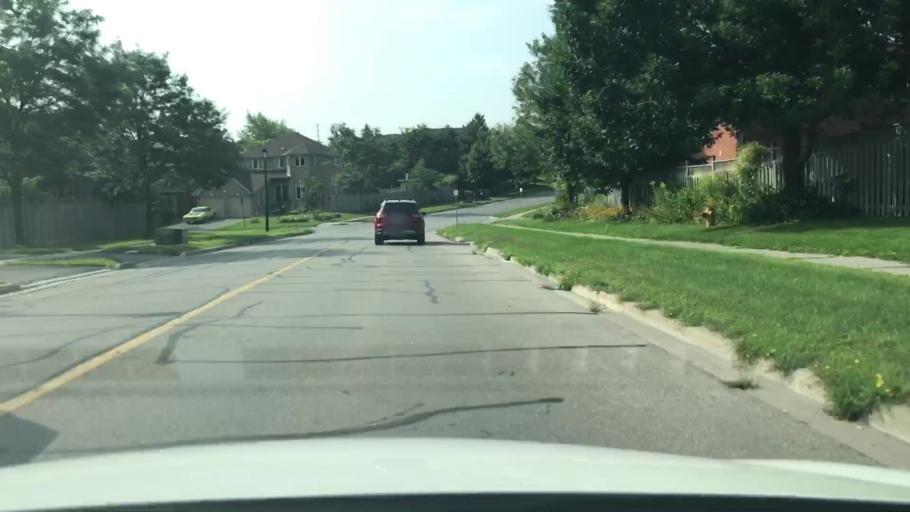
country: CA
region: Ontario
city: Newmarket
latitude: 44.0455
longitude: -79.4471
